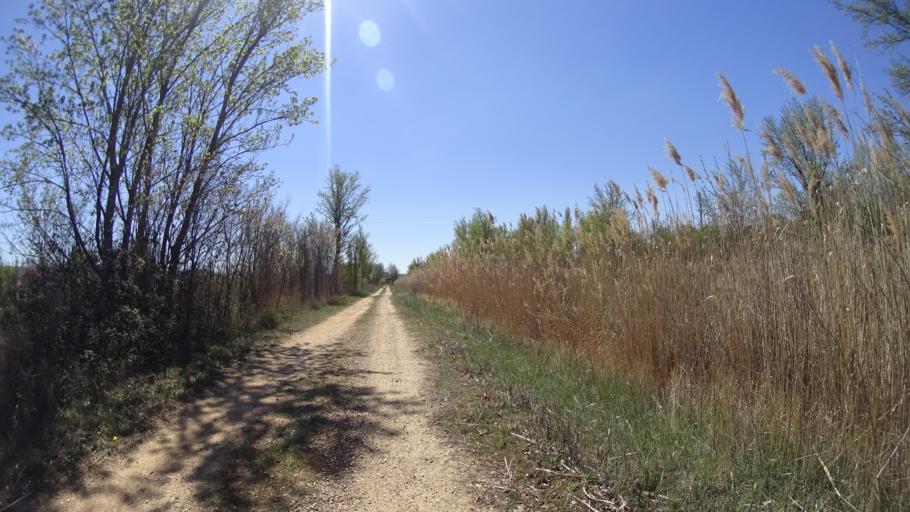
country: ES
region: Castille and Leon
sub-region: Provincia de Valladolid
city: Cubillas de Santa Marta
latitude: 41.8103
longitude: -4.5803
